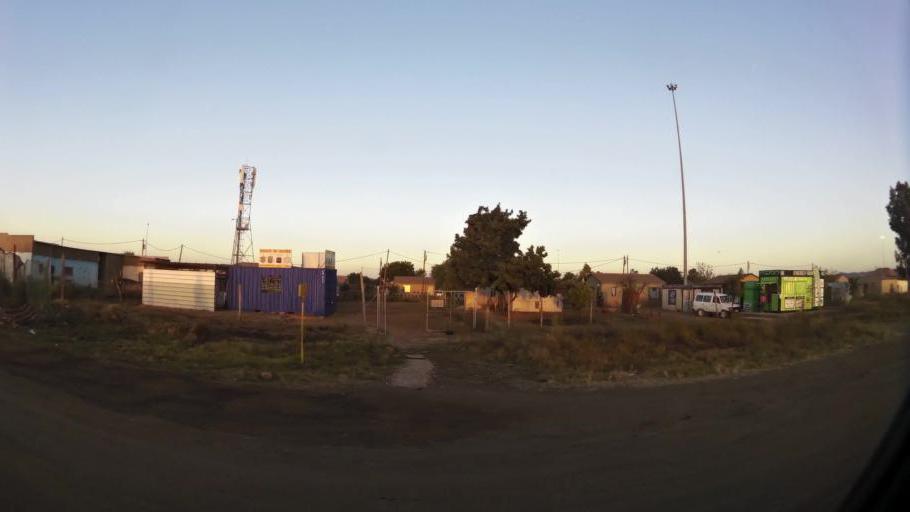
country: ZA
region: North-West
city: Ga-Rankuwa
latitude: -25.5857
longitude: 28.0458
